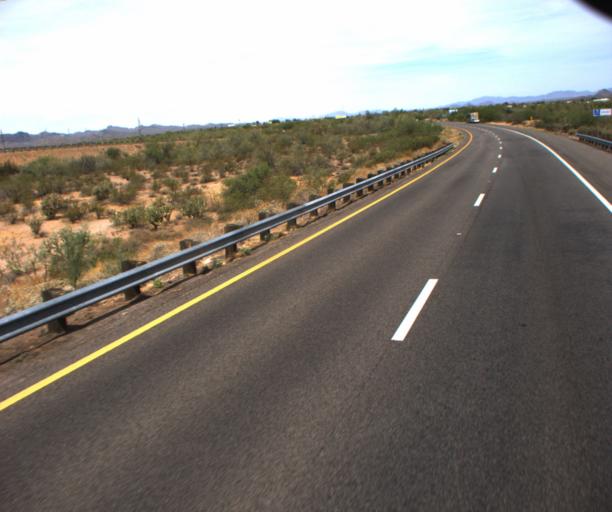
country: US
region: Arizona
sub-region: Maricopa County
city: Wickenburg
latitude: 33.8455
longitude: -112.6121
